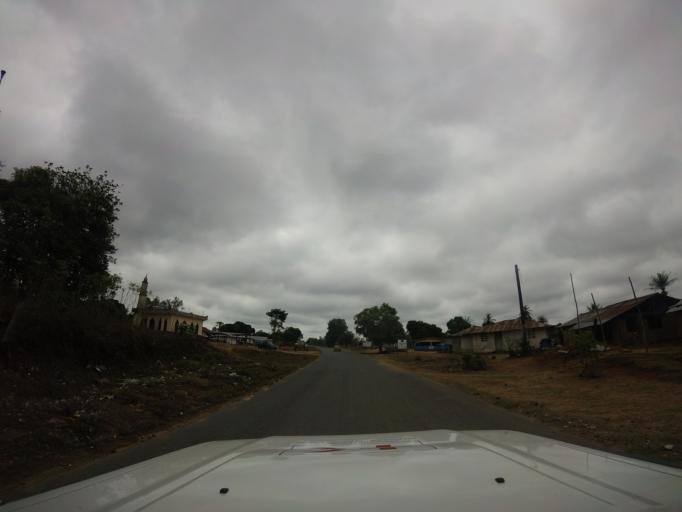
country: LR
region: Montserrado
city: Monrovia
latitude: 6.5728
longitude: -10.8813
